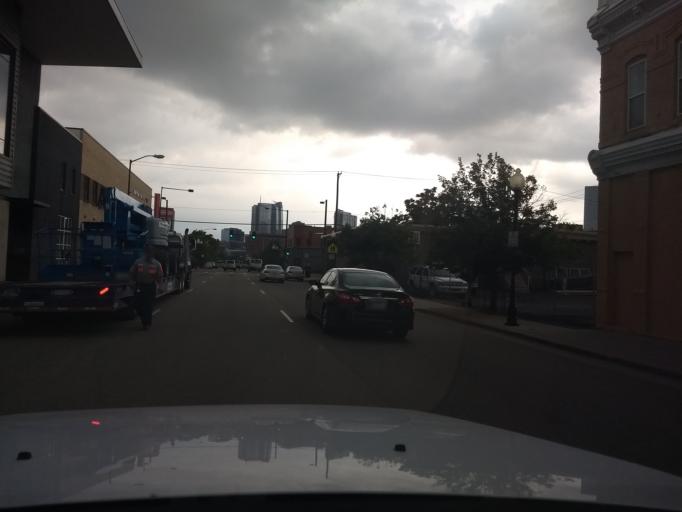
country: US
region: Colorado
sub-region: Denver County
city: Denver
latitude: 39.7330
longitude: -104.9987
